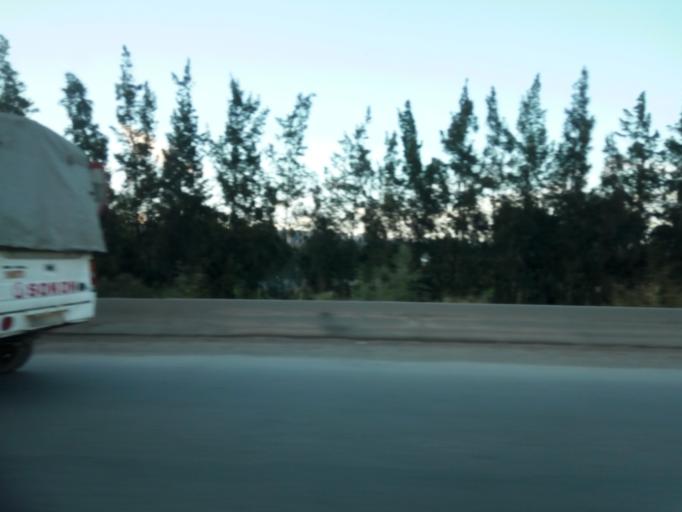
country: DZ
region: Tipaza
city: Baraki
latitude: 36.6785
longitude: 3.0649
